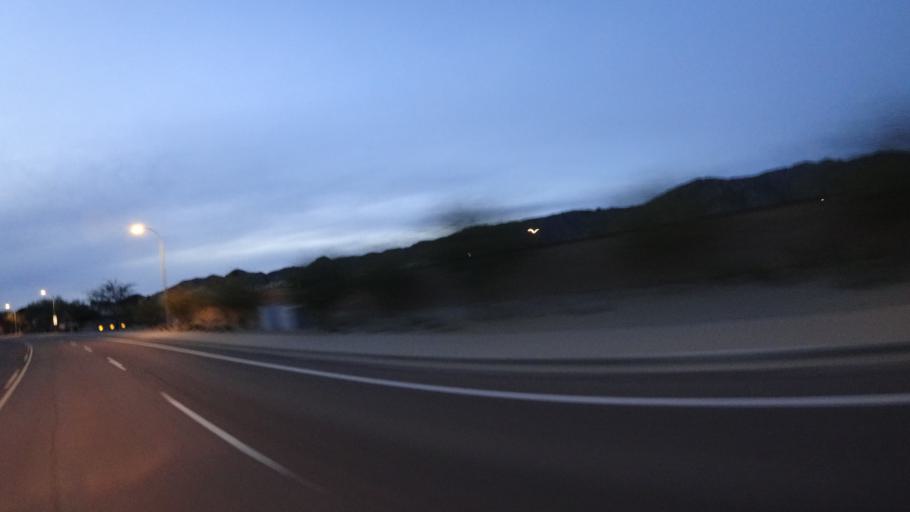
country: US
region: Arizona
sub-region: Maricopa County
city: Laveen
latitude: 33.3032
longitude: -112.0866
